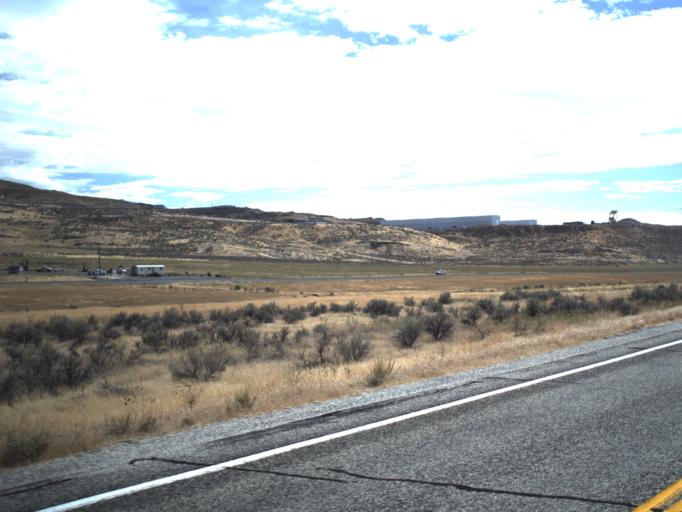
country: US
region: Utah
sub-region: Box Elder County
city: Tremonton
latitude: 41.6855
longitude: -112.4442
